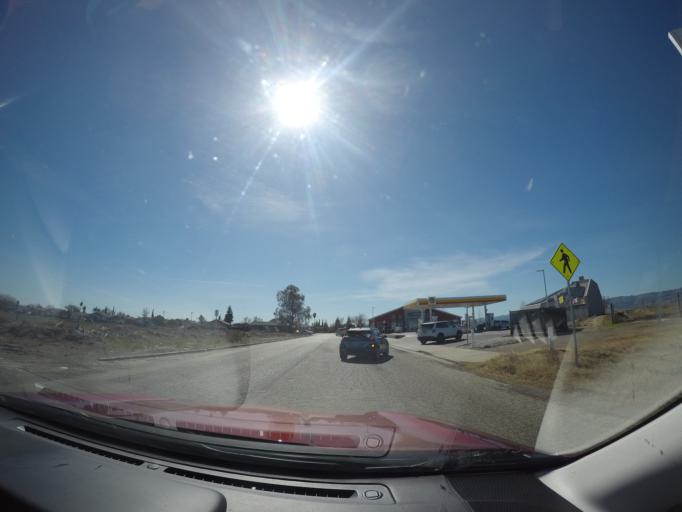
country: US
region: California
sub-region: Colusa County
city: Williams
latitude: 39.1607
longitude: -122.1612
